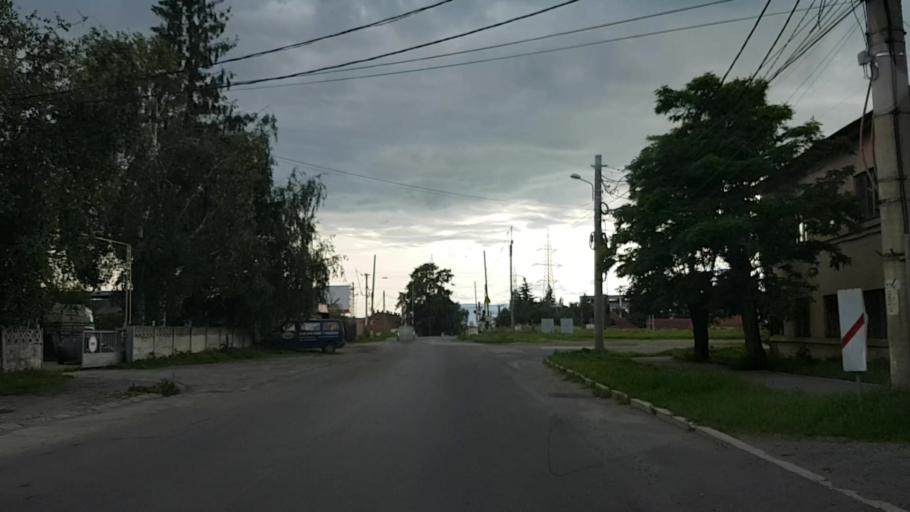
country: RO
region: Harghita
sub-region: Municipiul Gheorgheni
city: Gheorgheni
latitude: 46.7149
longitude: 25.5768
